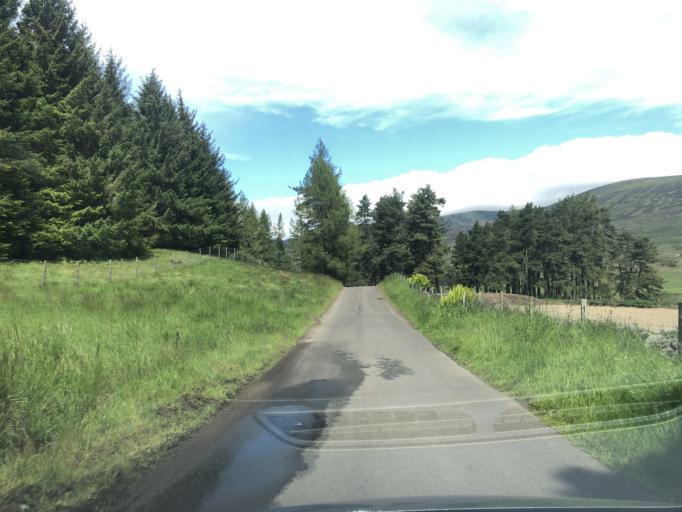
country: GB
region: Scotland
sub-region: Angus
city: Kirriemuir
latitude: 56.8173
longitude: -3.0579
